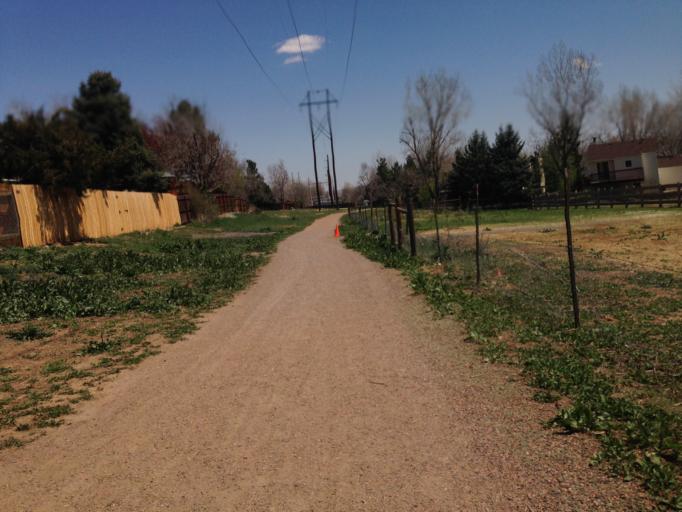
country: US
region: Colorado
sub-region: Boulder County
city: Louisville
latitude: 39.9906
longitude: -105.1170
